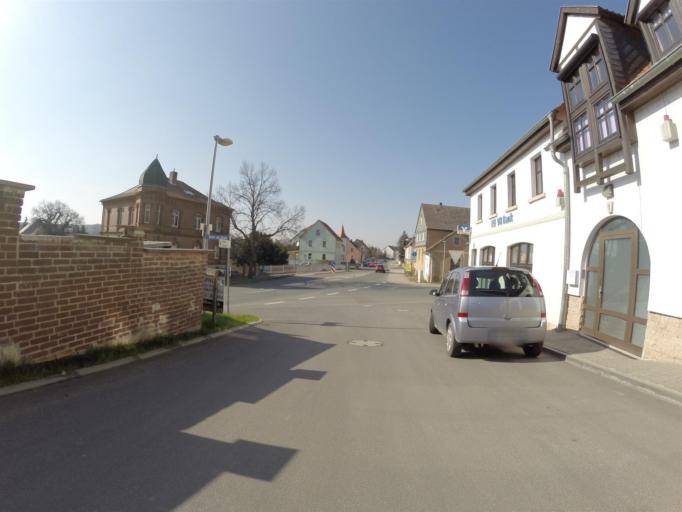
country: DE
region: Thuringia
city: Mellingen
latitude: 50.9437
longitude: 11.3935
